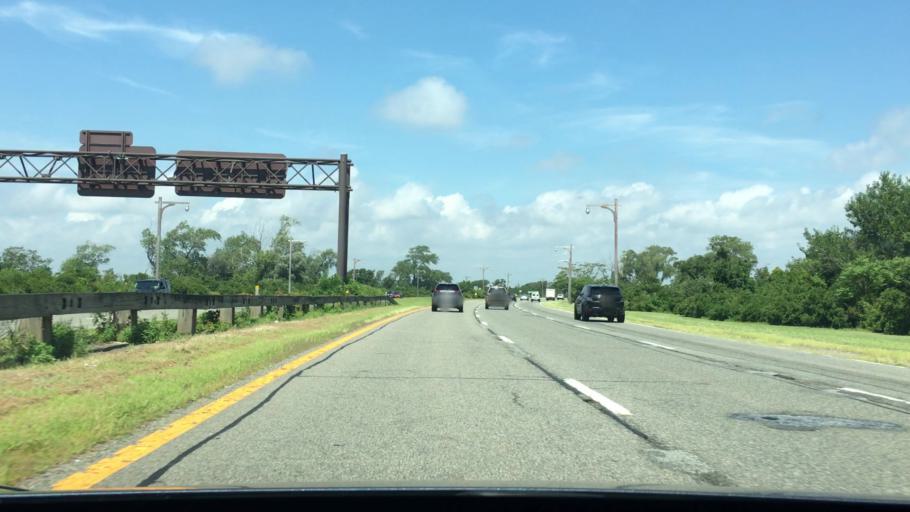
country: US
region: New York
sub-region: Nassau County
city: Point Lookout
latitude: 40.6181
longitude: -73.5577
